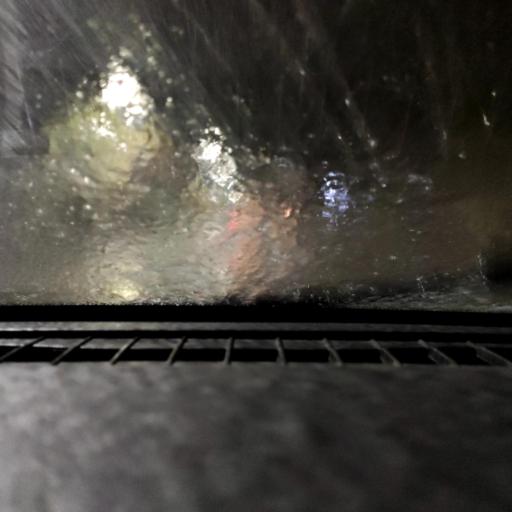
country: RU
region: Voronezj
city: Maslovka
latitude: 51.5929
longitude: 39.2436
